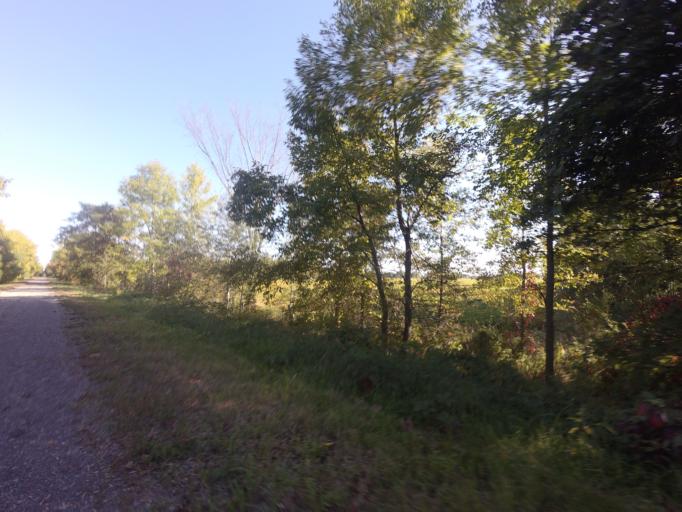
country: CA
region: Ontario
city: Hawkesbury
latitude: 45.5232
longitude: -74.5414
